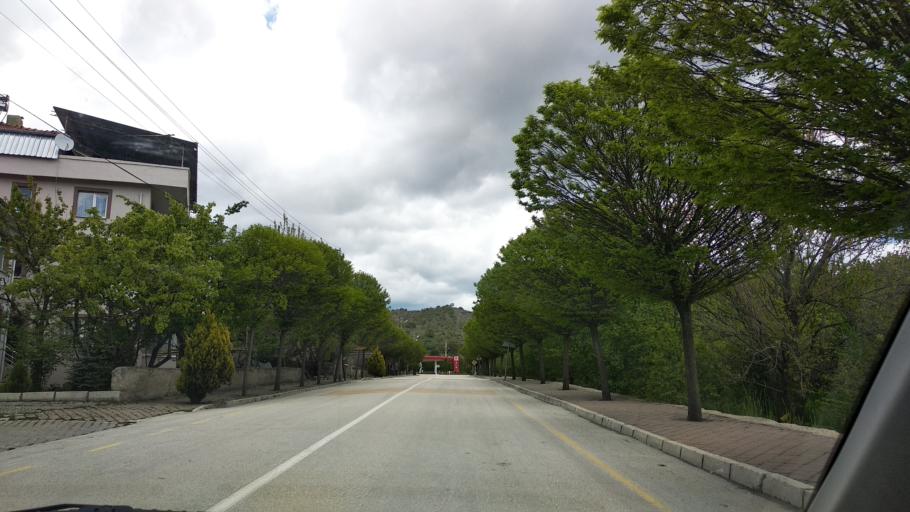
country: TR
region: Bolu
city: Seben
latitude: 40.4145
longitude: 31.5752
